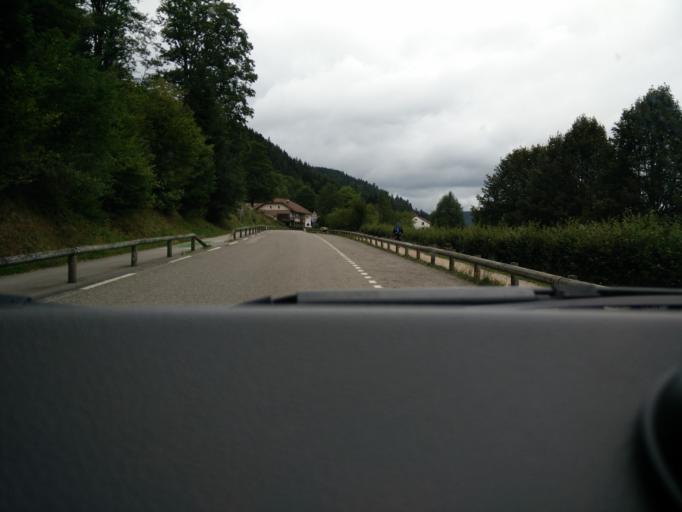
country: FR
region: Lorraine
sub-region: Departement des Vosges
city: Xonrupt-Longemer
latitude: 48.0664
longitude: 6.9498
